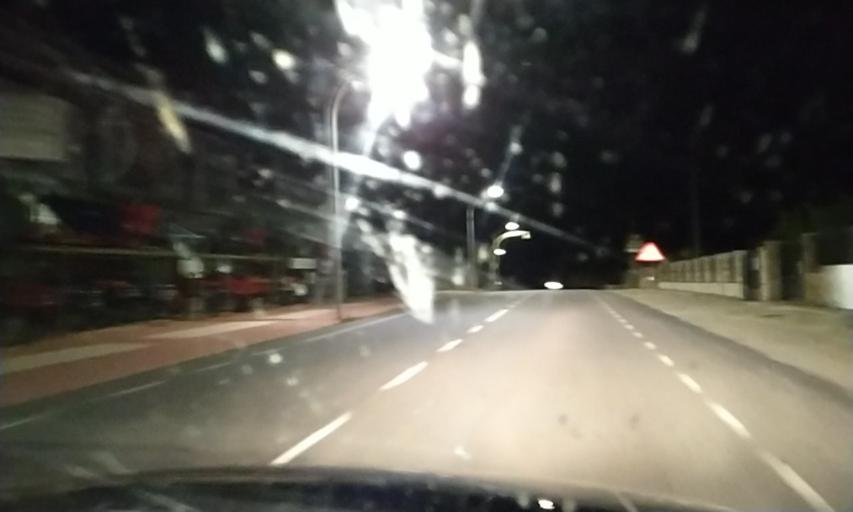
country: ES
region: Extremadura
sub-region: Provincia de Caceres
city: Perales del Puerto
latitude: 40.1603
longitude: -6.6829
